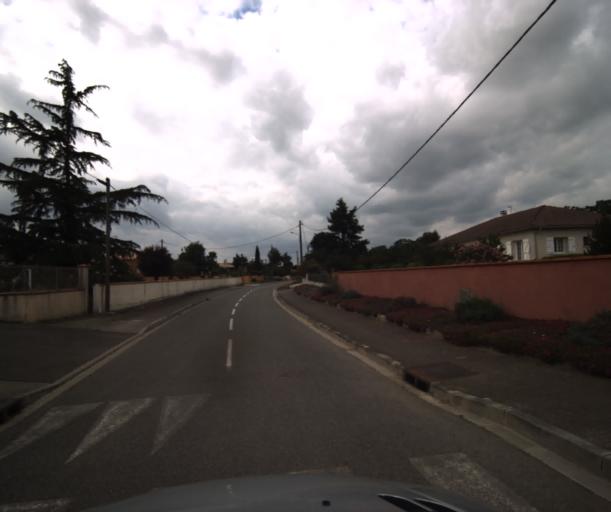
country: FR
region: Midi-Pyrenees
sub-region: Departement de la Haute-Garonne
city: Labarthe-sur-Leze
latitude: 43.4420
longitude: 1.3972
